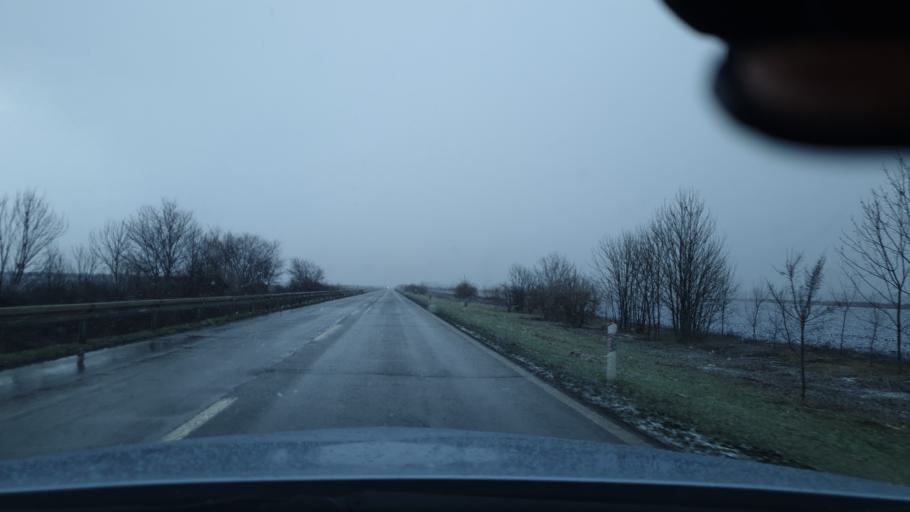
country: RS
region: Autonomna Pokrajina Vojvodina
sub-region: Juznobanatski Okrug
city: Pancevo
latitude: 44.8578
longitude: 20.7510
